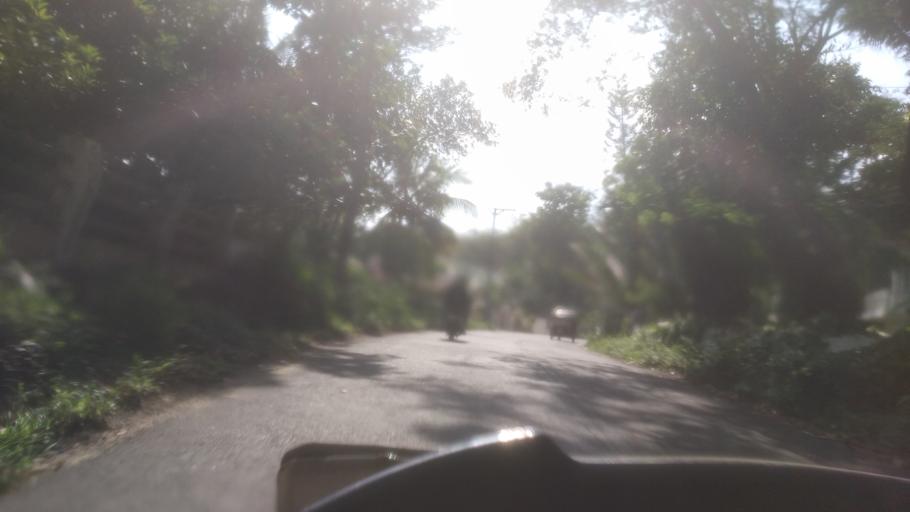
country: IN
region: Kerala
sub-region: Ernakulam
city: Kotamangalam
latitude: 10.0014
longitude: 76.7283
